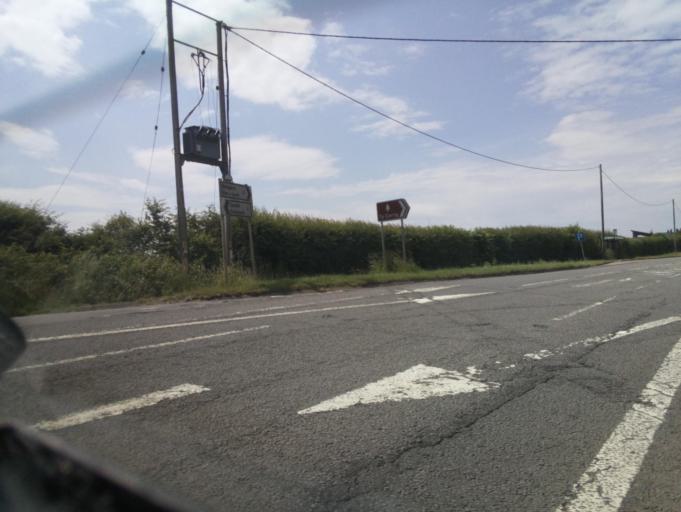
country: GB
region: Wales
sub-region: Vale of Glamorgan
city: Rhoose
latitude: 51.4573
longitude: -3.3640
